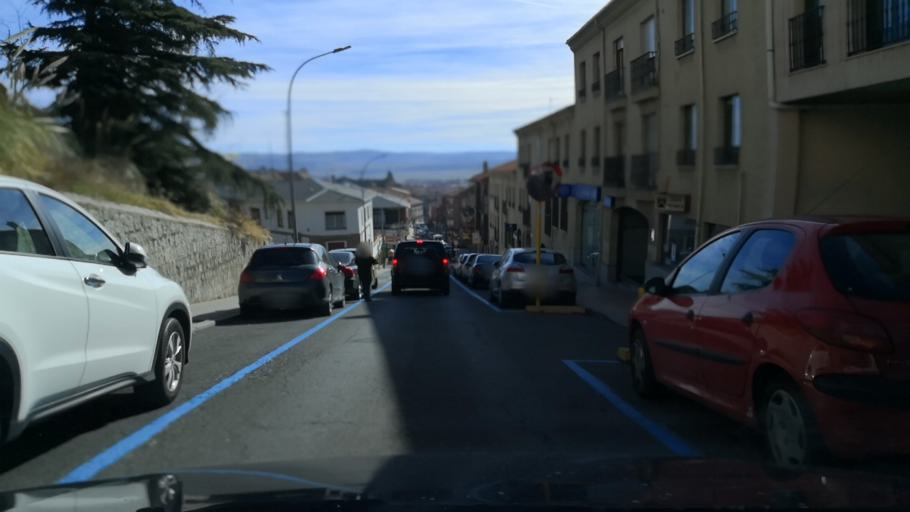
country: ES
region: Castille and Leon
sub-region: Provincia de Avila
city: Avila
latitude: 40.6538
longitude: -4.6933
